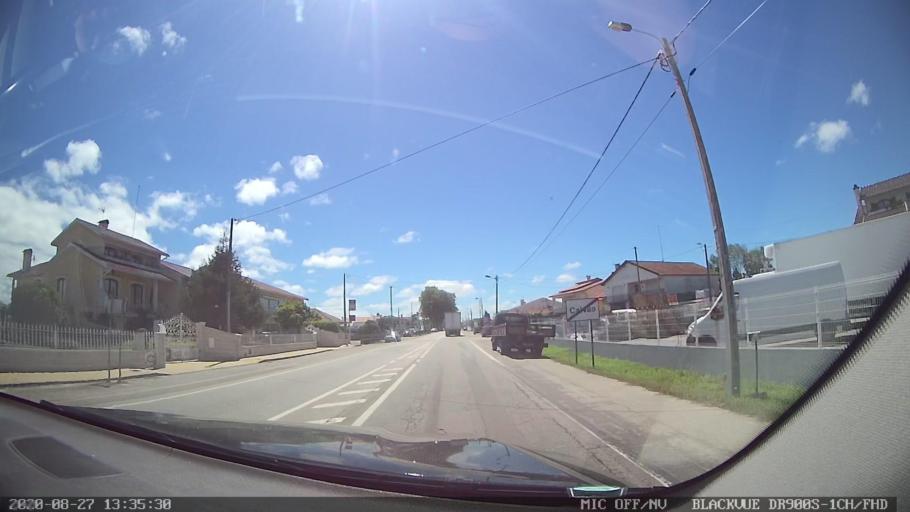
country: PT
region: Coimbra
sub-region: Mira
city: Mira
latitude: 40.4631
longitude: -8.7006
